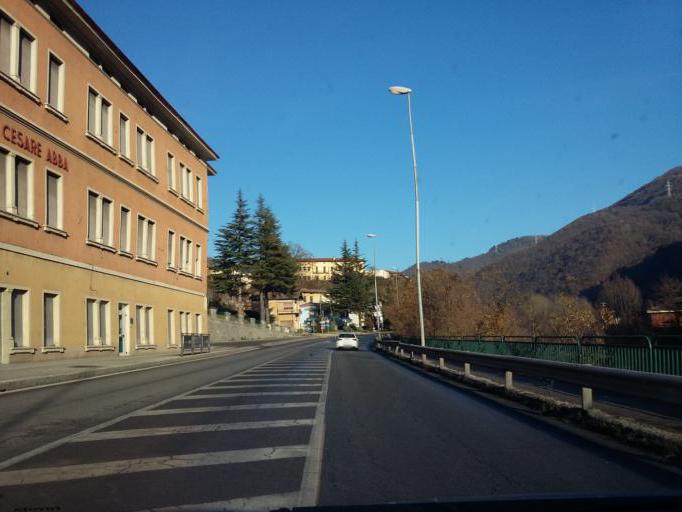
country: IT
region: Lombardy
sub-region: Provincia di Brescia
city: Vestone
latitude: 45.7111
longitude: 10.4062
